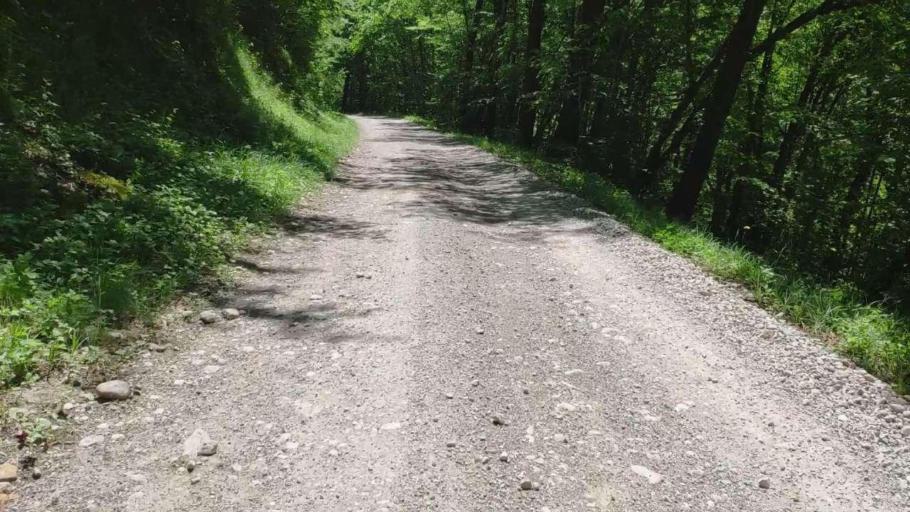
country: FR
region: Franche-Comte
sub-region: Departement du Jura
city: Perrigny
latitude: 46.7332
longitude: 5.6566
